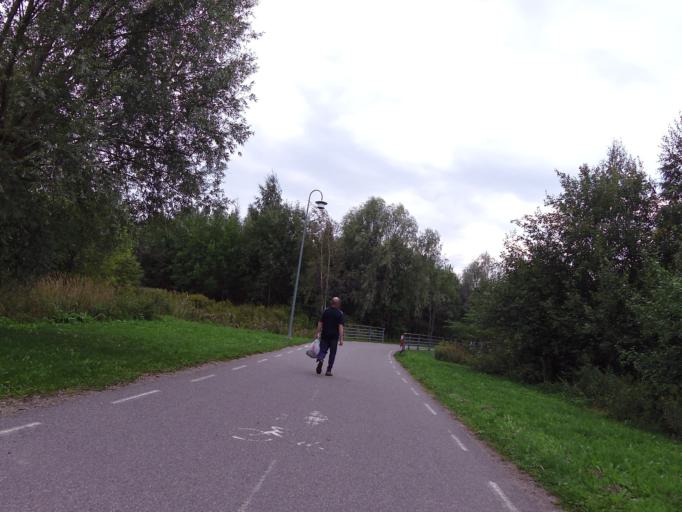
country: EE
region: Harju
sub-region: Tallinna linn
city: Tallinn
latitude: 59.4335
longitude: 24.6787
